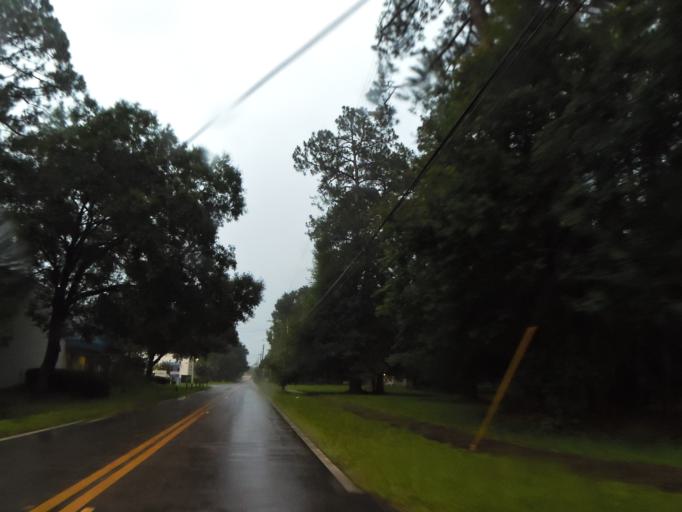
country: US
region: Florida
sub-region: Duval County
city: Jacksonville
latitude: 30.3142
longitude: -81.7386
